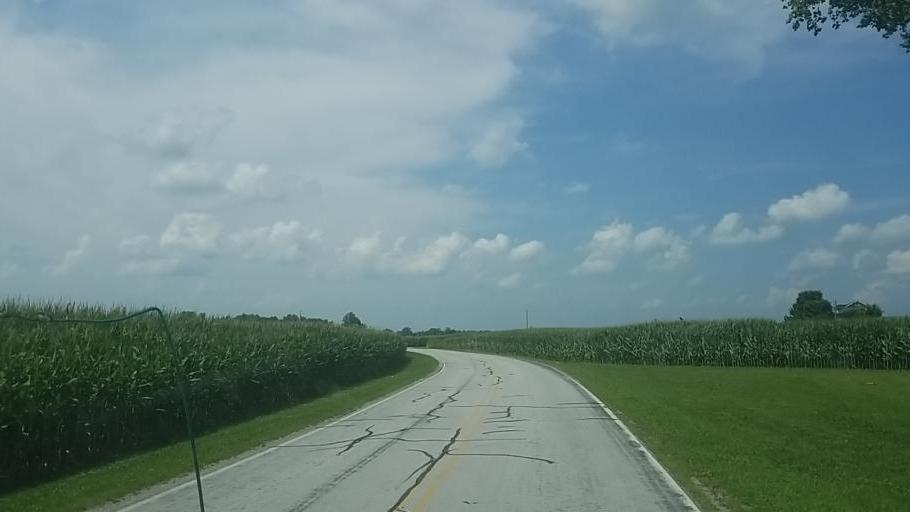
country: US
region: Ohio
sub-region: Hardin County
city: Kenton
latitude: 40.6923
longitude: -83.5739
